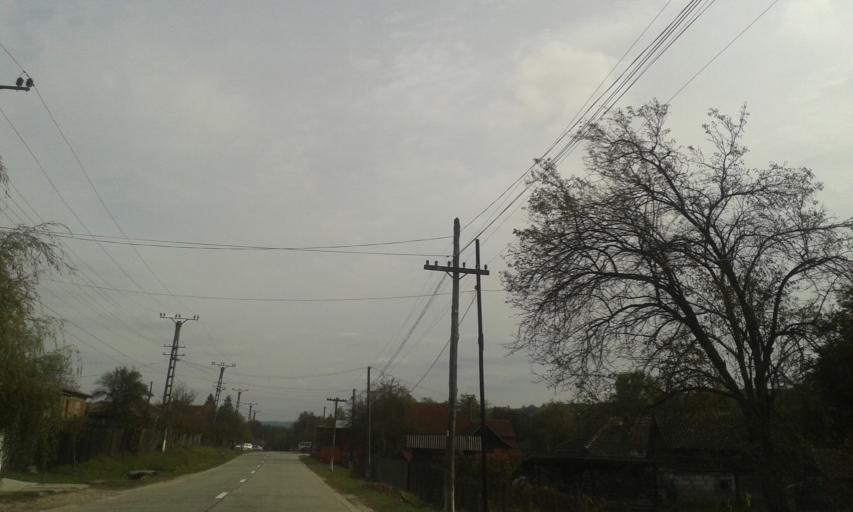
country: RO
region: Valcea
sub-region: Comuna Gradistea
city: Gradistea
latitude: 44.9115
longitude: 23.7854
